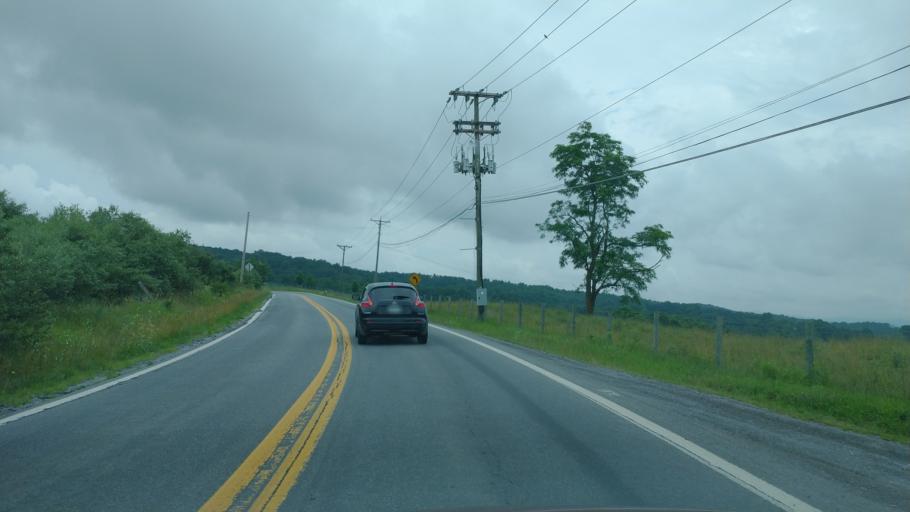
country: US
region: West Virginia
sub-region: Mercer County
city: Athens
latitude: 37.4142
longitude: -81.0200
